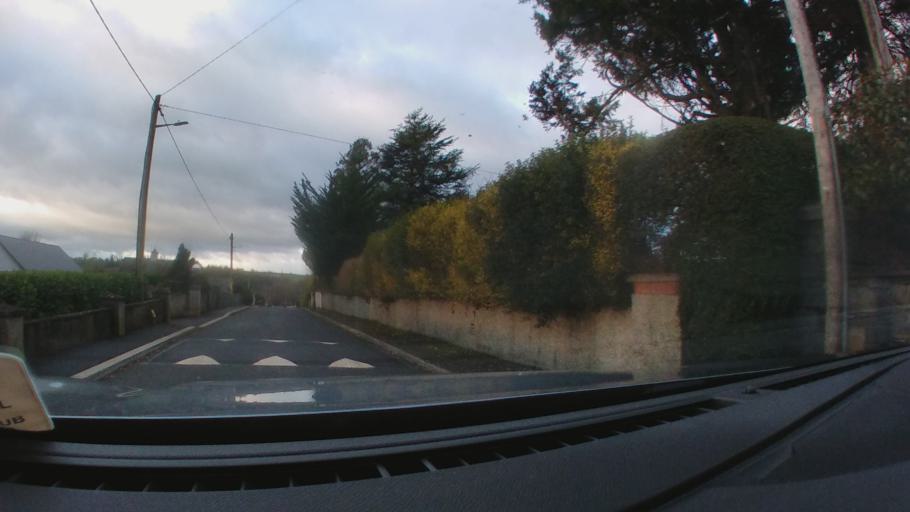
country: IE
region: Leinster
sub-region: Kilkenny
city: Thomastown
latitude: 52.5893
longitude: -7.1771
